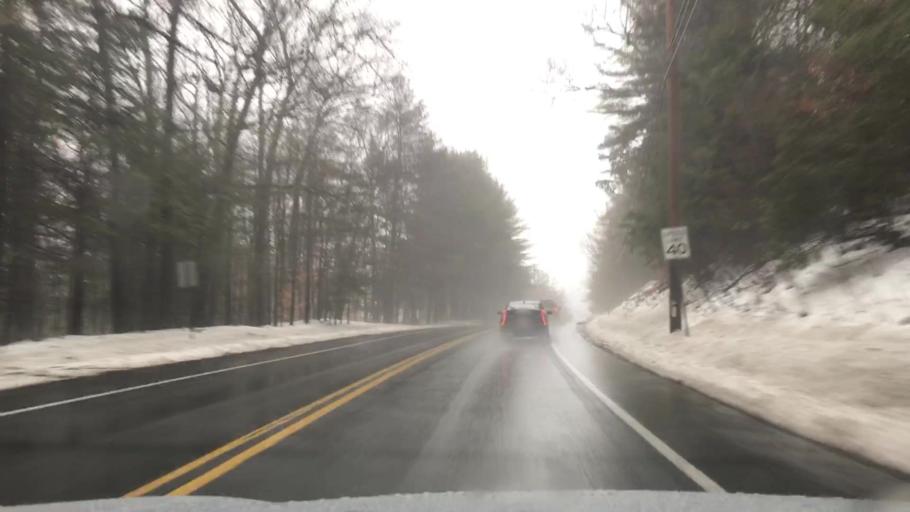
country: US
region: Massachusetts
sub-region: Franklin County
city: Wendell
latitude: 42.5023
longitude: -72.3371
